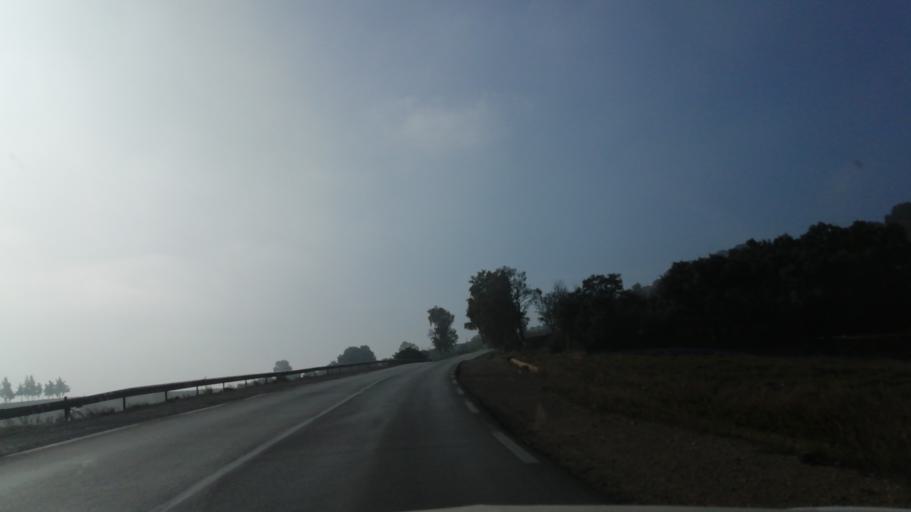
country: DZ
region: Mascara
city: Mascara
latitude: 35.5295
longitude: 0.3542
